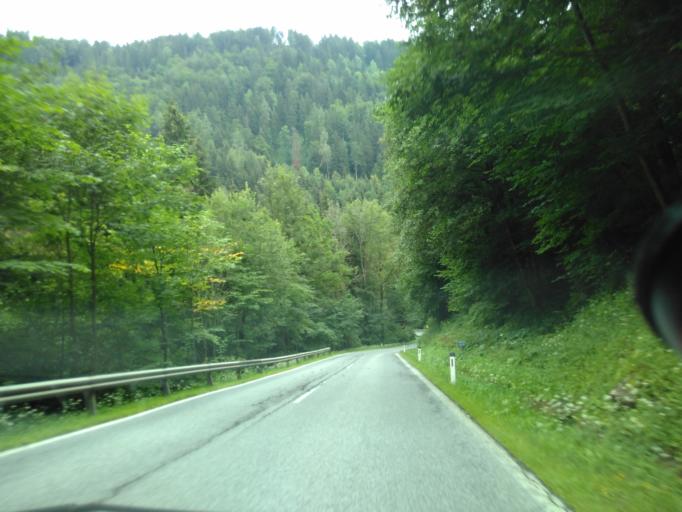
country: AT
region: Styria
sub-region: Politischer Bezirk Graz-Umgebung
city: Rothelstein
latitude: 47.2819
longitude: 15.3965
